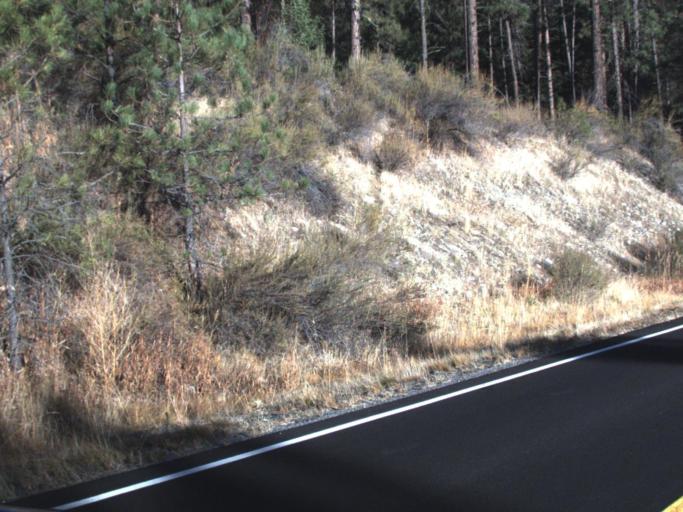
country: US
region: Washington
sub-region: Okanogan County
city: Coulee Dam
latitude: 48.0341
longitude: -118.6742
